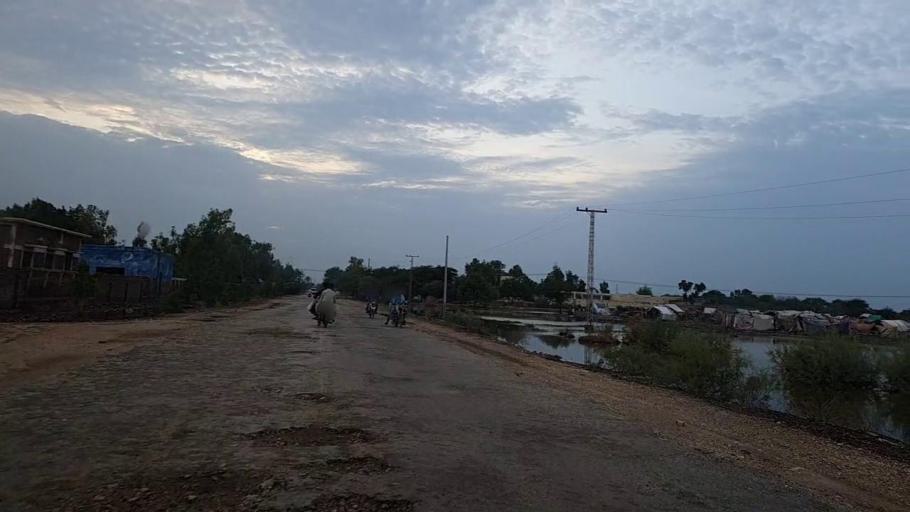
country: PK
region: Sindh
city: Naushahro Firoz
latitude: 26.8290
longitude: 68.1444
